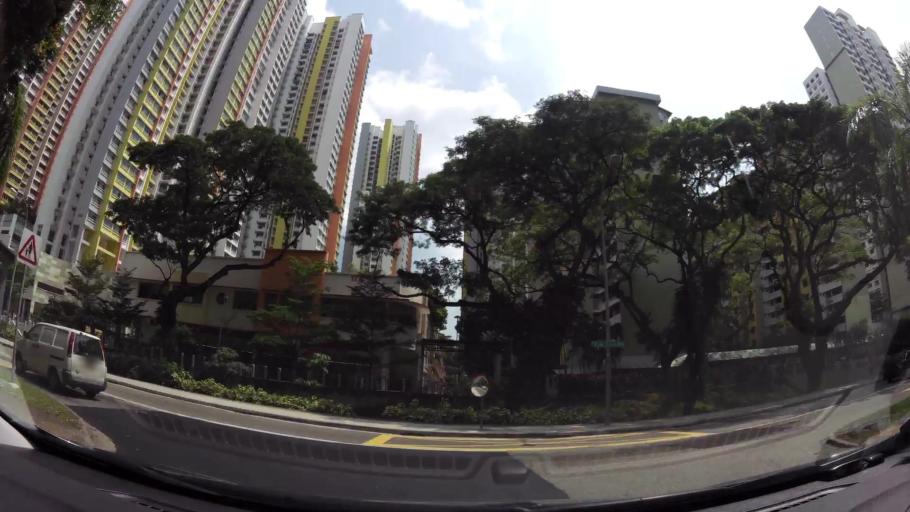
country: SG
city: Singapore
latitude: 1.2821
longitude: 103.8285
